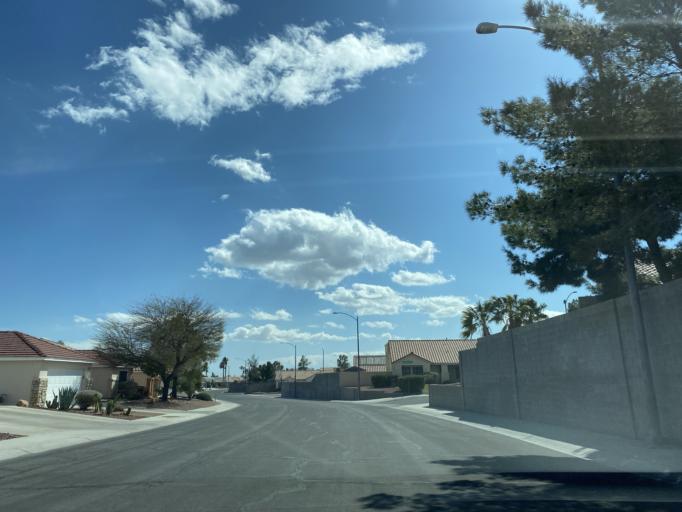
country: US
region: Nevada
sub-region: Clark County
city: Summerlin South
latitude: 36.2276
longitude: -115.3070
